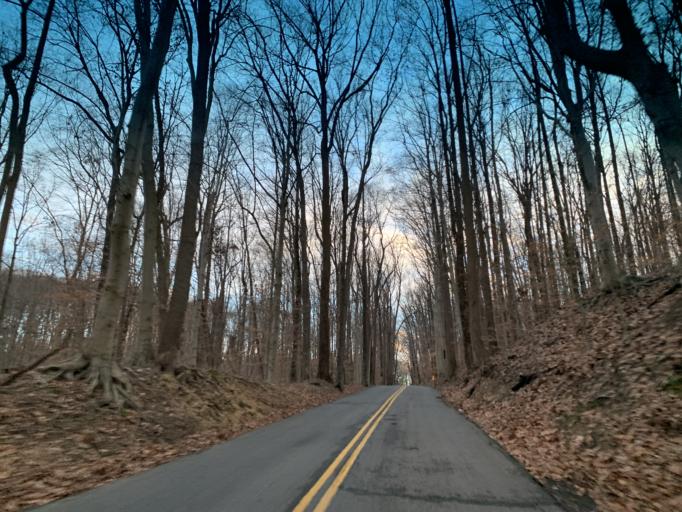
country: US
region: Maryland
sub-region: Harford County
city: Bel Air North
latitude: 39.6053
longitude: -76.3203
